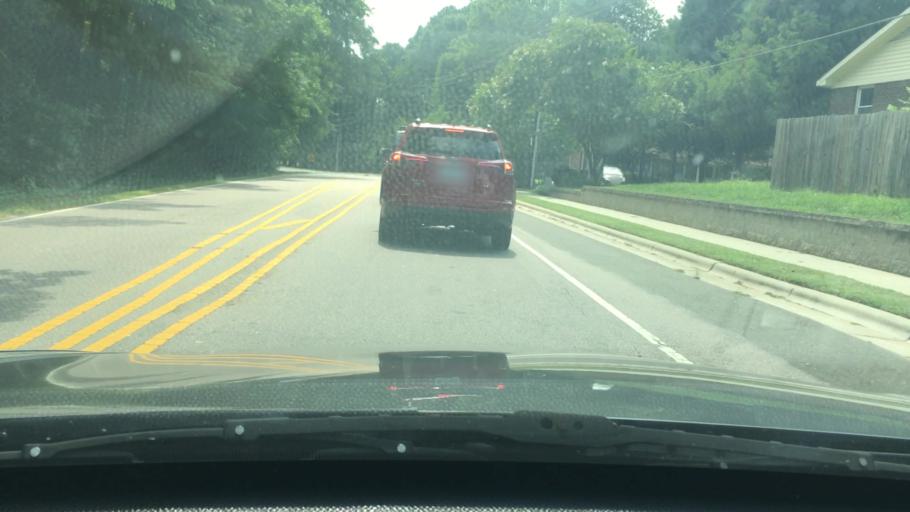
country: US
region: North Carolina
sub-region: Wake County
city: Cary
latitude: 35.7861
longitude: -78.7967
